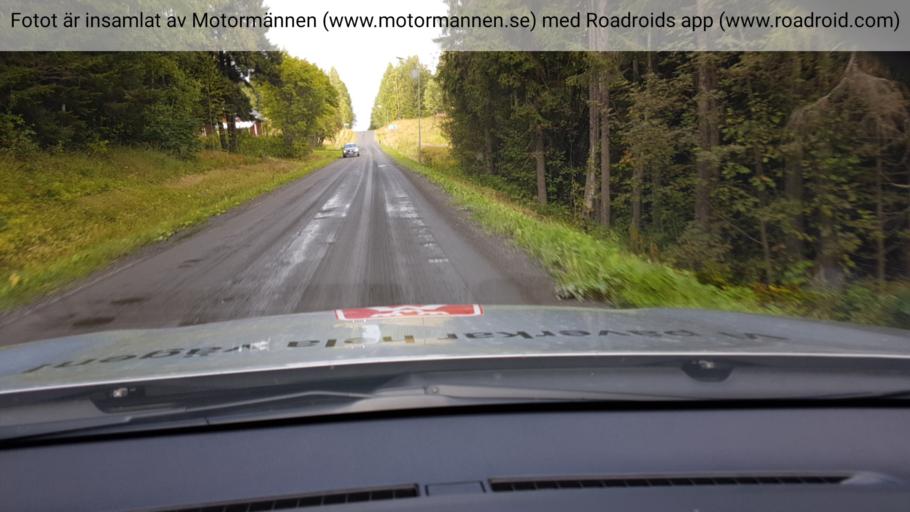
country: SE
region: Jaemtland
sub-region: Stroemsunds Kommun
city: Stroemsund
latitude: 64.0869
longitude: 15.8244
